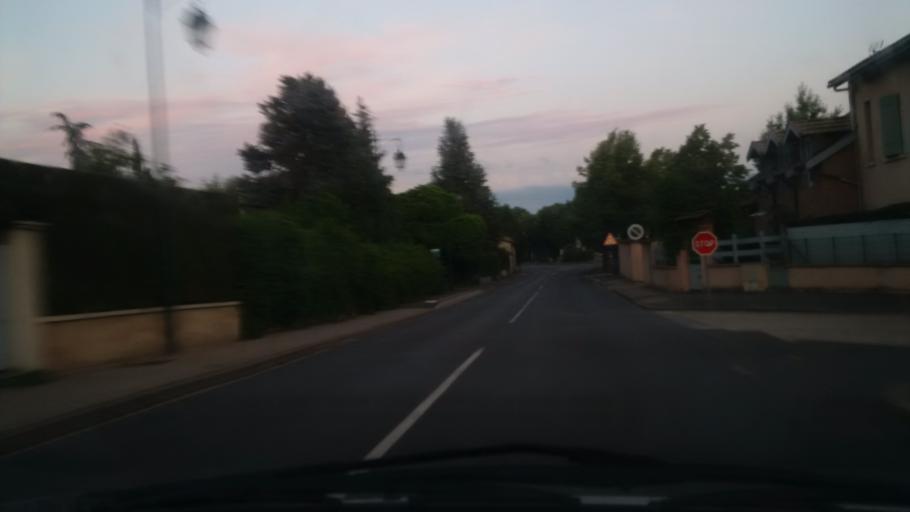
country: FR
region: Rhone-Alpes
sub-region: Departement de l'Ain
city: Trevoux
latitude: 45.9414
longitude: 4.7681
